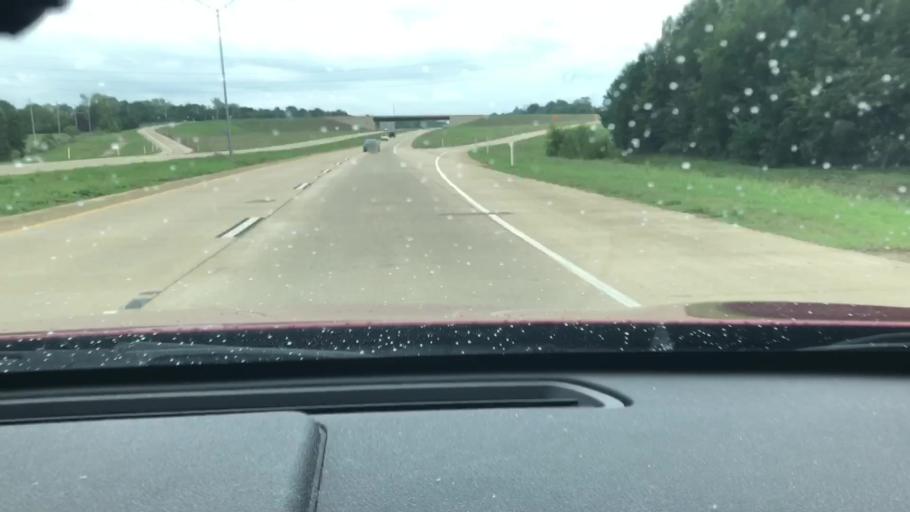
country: US
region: Texas
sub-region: Bowie County
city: Texarkana
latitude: 33.3854
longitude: -94.0489
